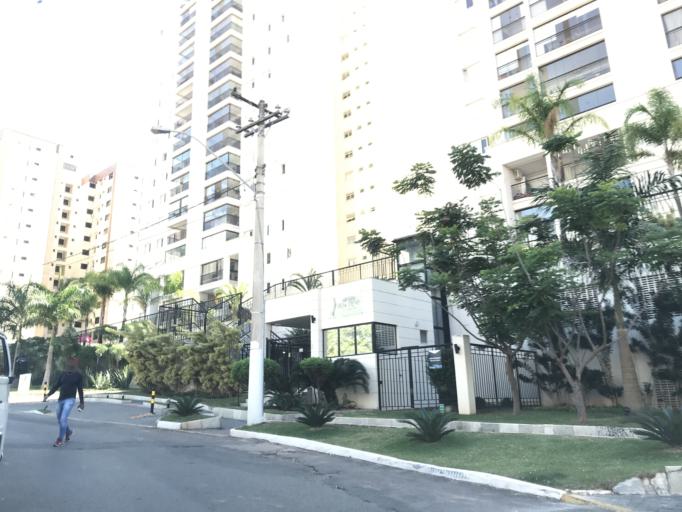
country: BR
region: Federal District
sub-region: Brasilia
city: Brasilia
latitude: -15.8359
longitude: -48.0281
